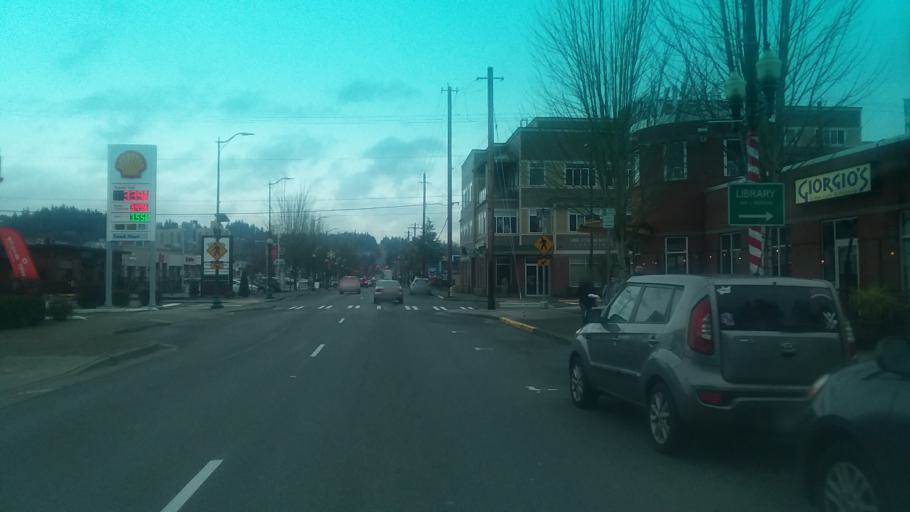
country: US
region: Washington
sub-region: Pierce County
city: Puyallup
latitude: 47.1889
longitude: -122.2938
